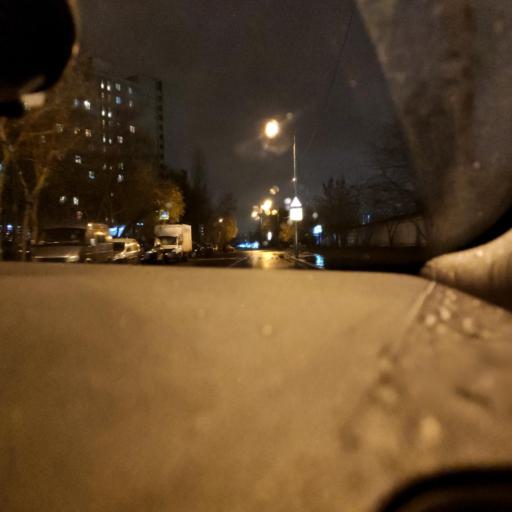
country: RU
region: Moscow
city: Strogino
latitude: 55.8597
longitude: 37.4082
